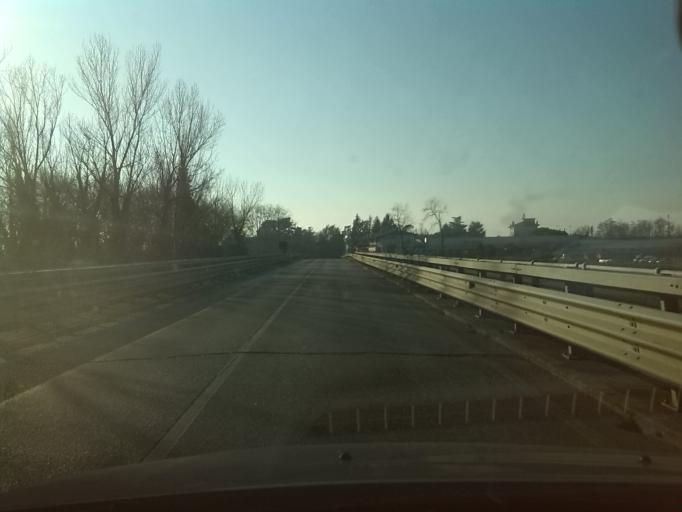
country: IT
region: Friuli Venezia Giulia
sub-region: Provincia di Udine
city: Percoto
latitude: 45.9775
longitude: 13.3323
